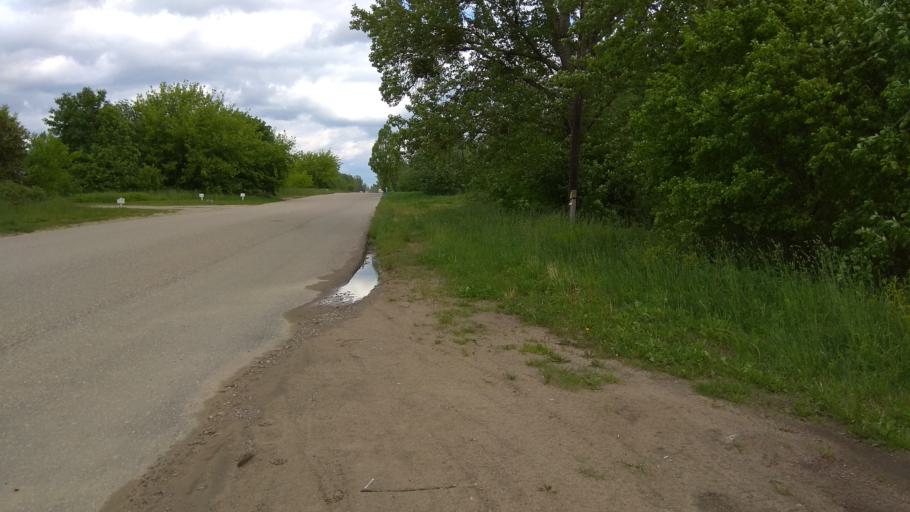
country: BY
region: Grodnenskaya
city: Hrodna
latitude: 53.7127
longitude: 23.7972
